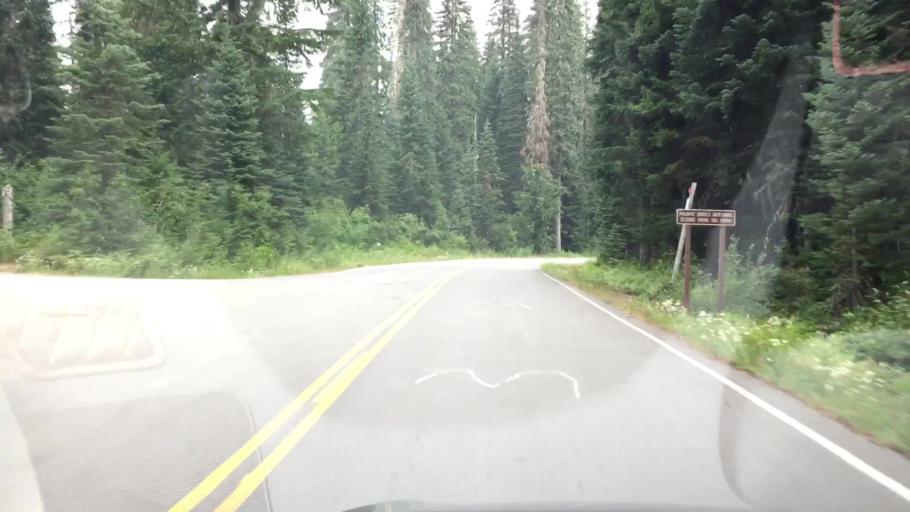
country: US
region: Washington
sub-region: Klickitat County
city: White Salmon
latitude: 46.1617
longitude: -121.6317
